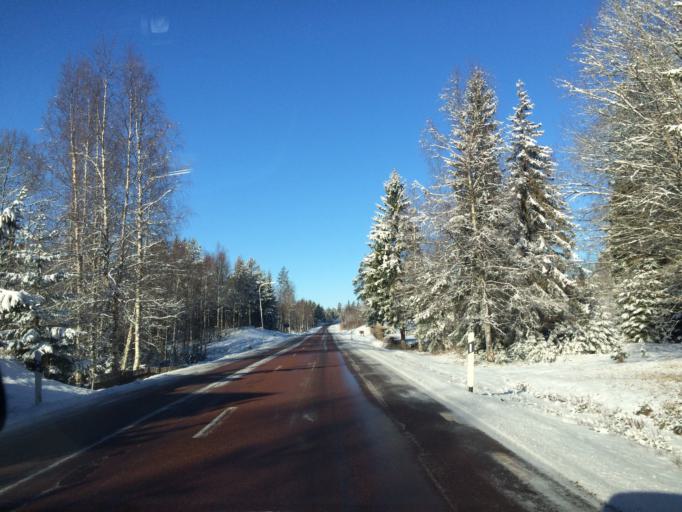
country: SE
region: Dalarna
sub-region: Vansbro Kommun
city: Vansbro
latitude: 60.8444
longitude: 14.1845
